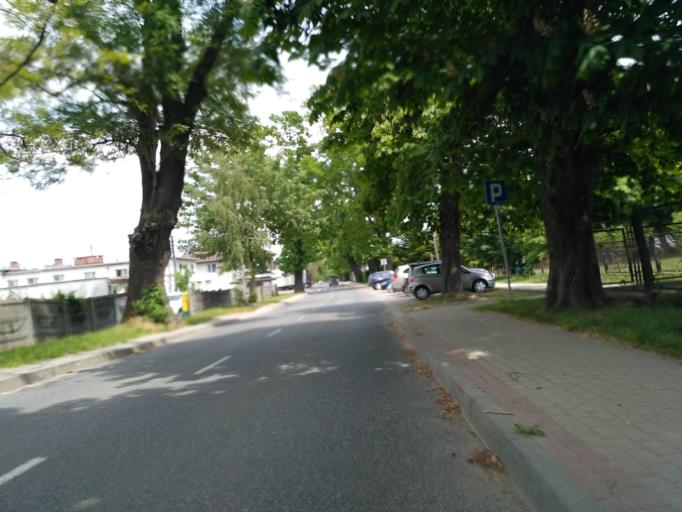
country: PL
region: Subcarpathian Voivodeship
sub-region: Powiat krosnienski
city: Odrzykon
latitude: 49.6994
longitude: 21.7145
